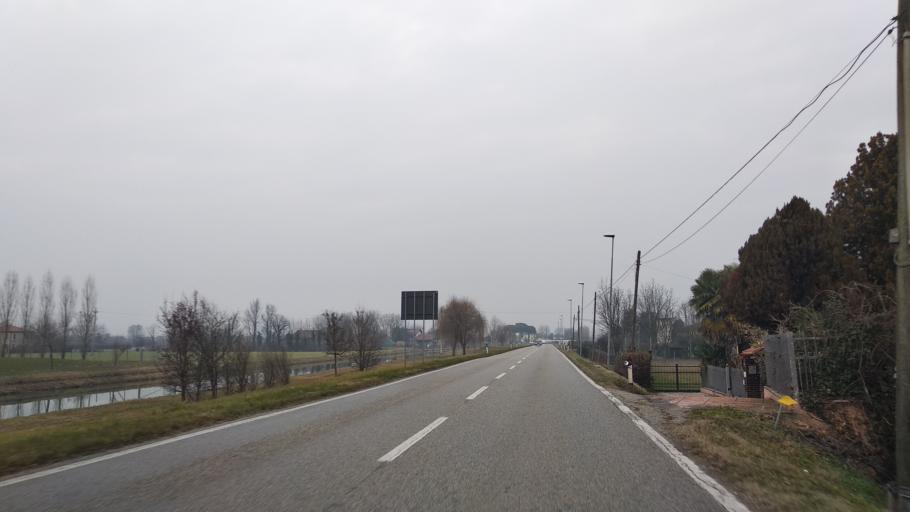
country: IT
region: Veneto
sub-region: Provincia di Padova
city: Santa Maria di Non
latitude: 45.5167
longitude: 11.8658
